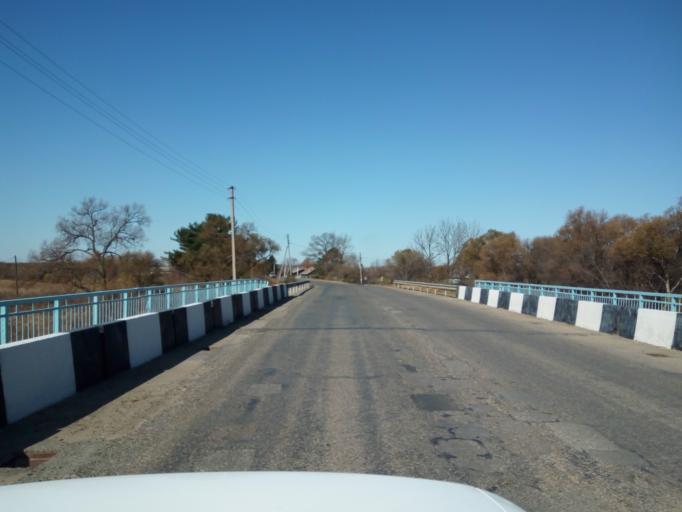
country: RU
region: Primorskiy
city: Dal'nerechensk
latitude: 45.9141
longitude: 133.7896
